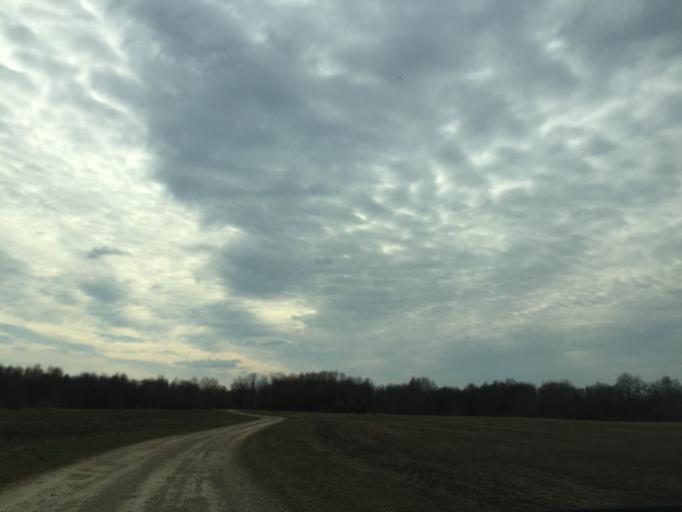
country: EE
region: Ida-Virumaa
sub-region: Sillamaee linn
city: Sillamae
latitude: 59.3875
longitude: 27.9000
